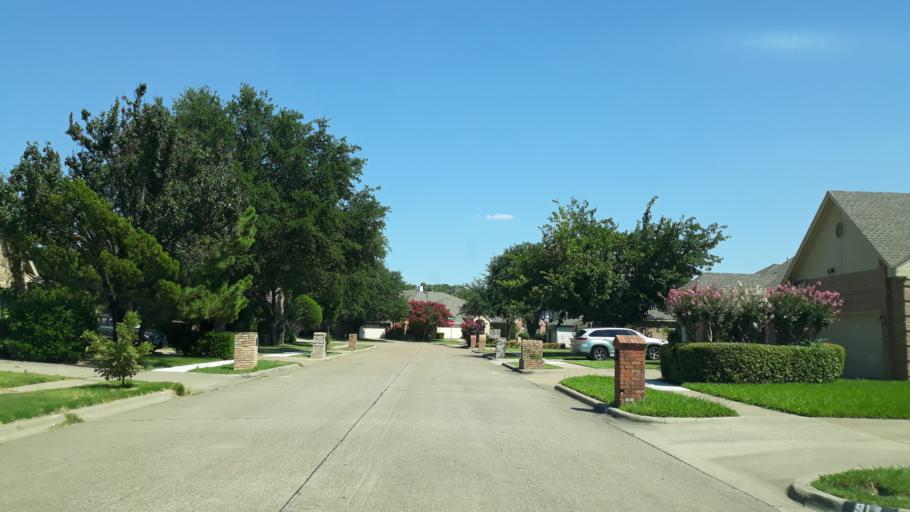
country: US
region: Texas
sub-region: Dallas County
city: Irving
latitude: 32.8229
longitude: -97.0086
